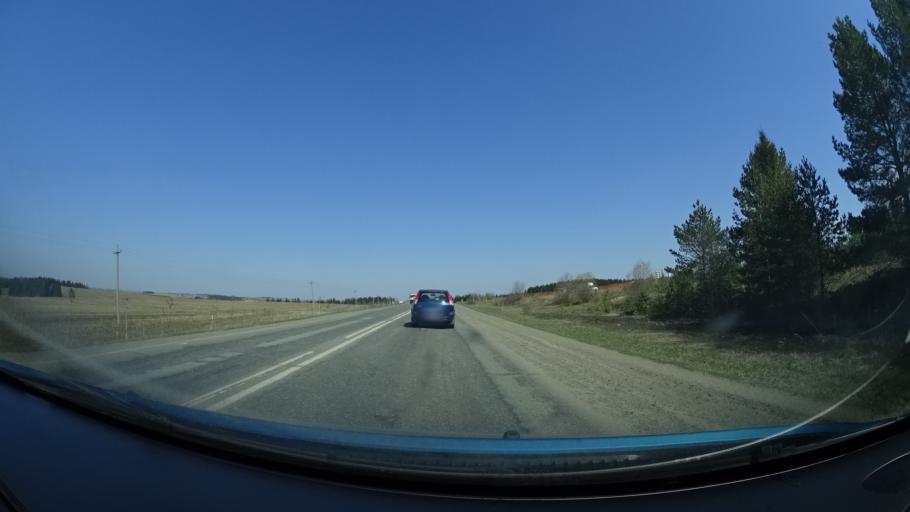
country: RU
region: Perm
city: Kultayevo
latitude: 57.8593
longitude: 55.8677
